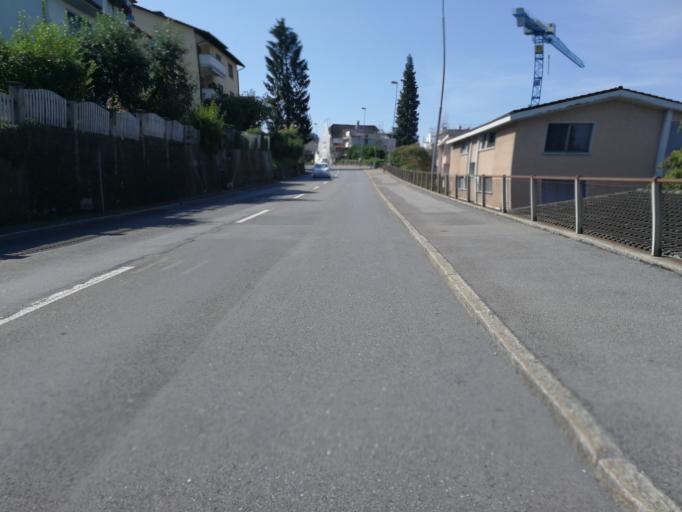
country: CH
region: Schwyz
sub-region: Bezirk Kuessnacht
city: Kussnacht
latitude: 47.0774
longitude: 8.4401
